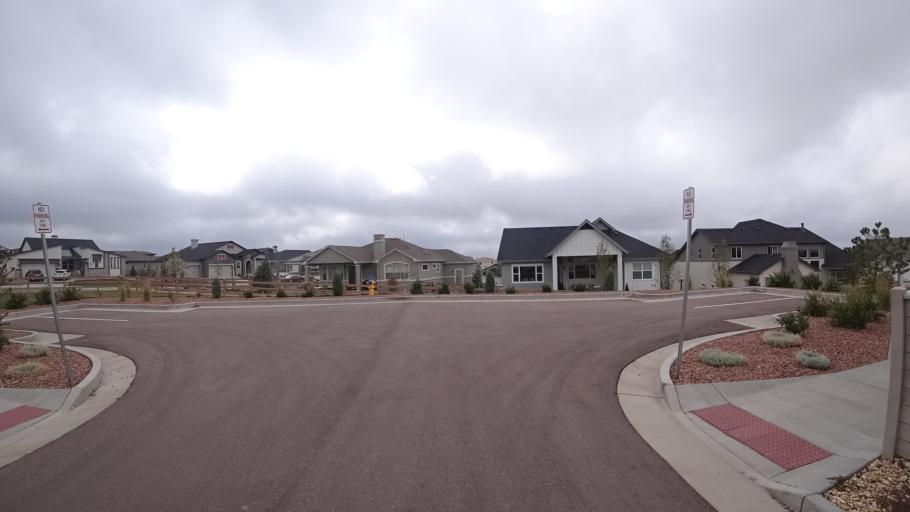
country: US
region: Colorado
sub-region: El Paso County
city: Gleneagle
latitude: 39.0093
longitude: -104.7901
